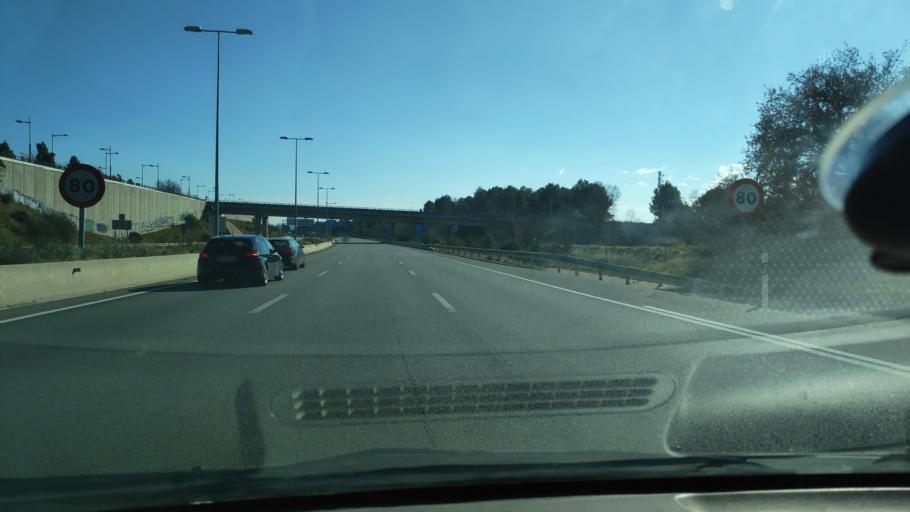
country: ES
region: Catalonia
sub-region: Provincia de Barcelona
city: Sant Quirze del Valles
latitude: 41.5462
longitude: 2.0770
